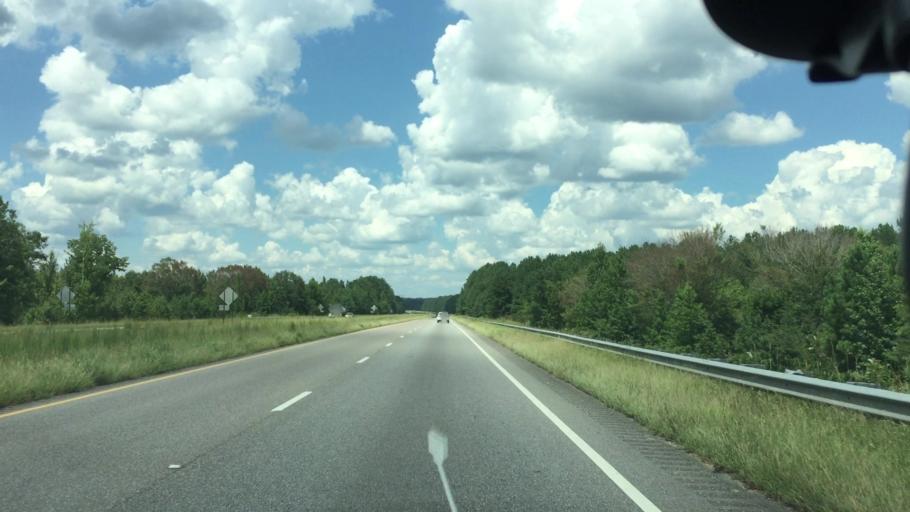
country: US
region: Alabama
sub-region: Pike County
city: Troy
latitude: 31.9817
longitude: -86.0267
